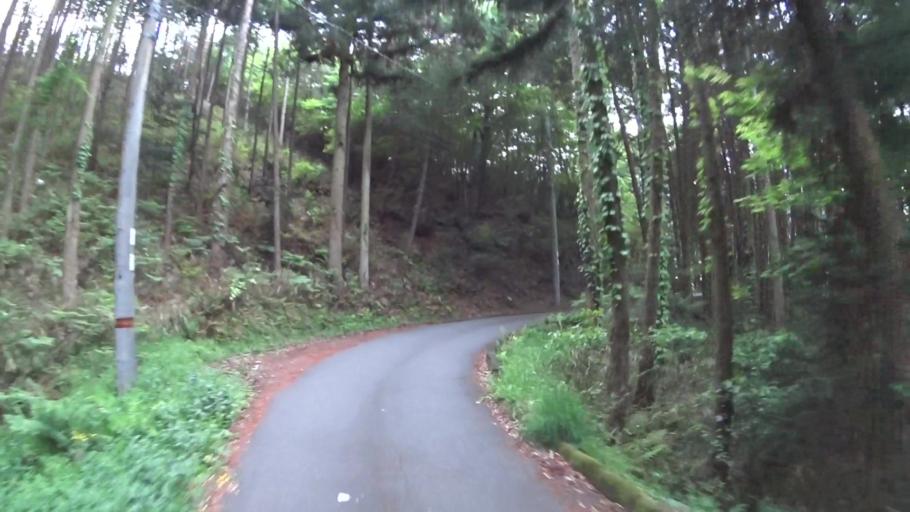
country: JP
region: Kyoto
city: Kameoka
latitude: 35.0635
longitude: 135.5352
